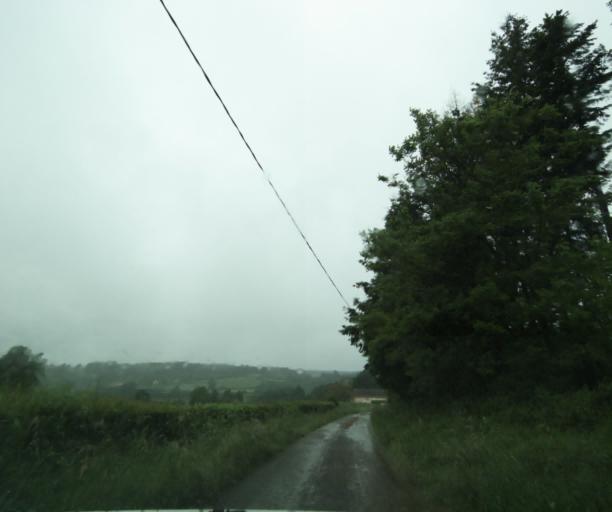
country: FR
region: Bourgogne
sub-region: Departement de Saone-et-Loire
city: Charolles
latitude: 46.3885
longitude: 4.3306
